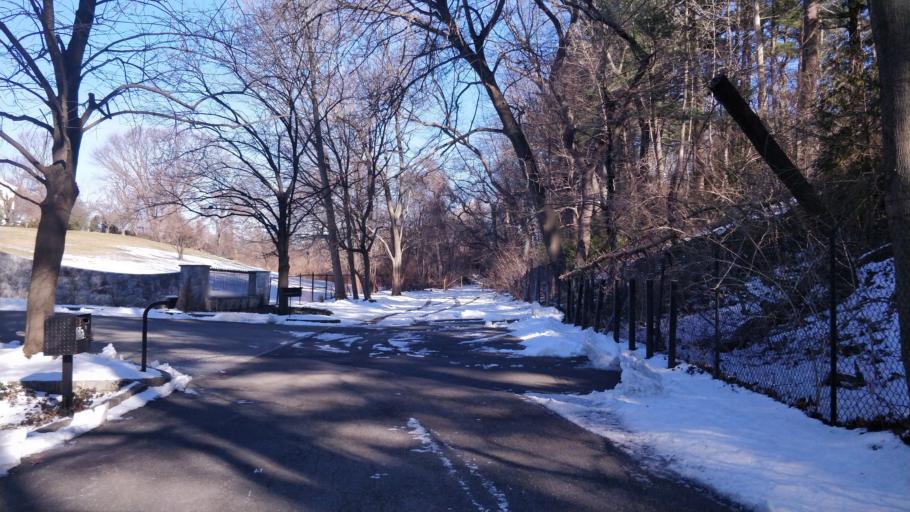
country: US
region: New York
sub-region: Nassau County
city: Old Brookville
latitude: 40.8387
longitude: -73.6085
